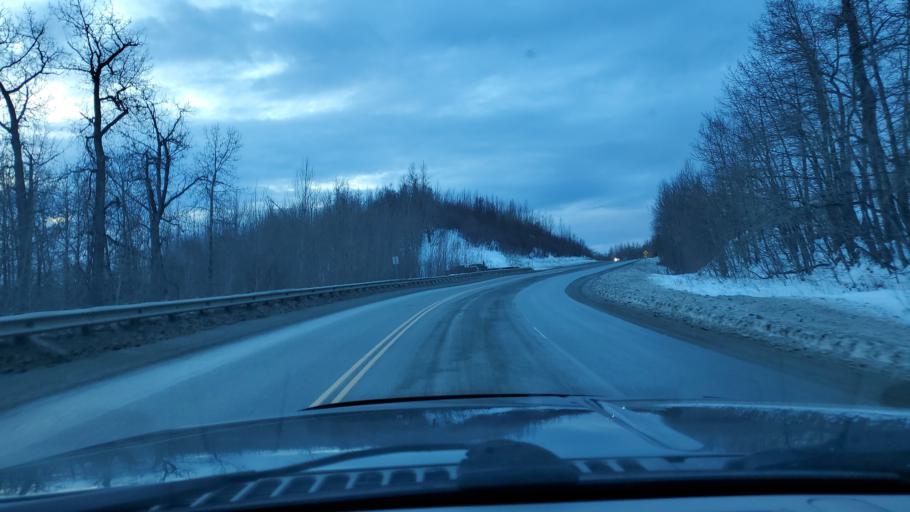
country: US
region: Alaska
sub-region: Matanuska-Susitna Borough
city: Lazy Mountain
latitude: 61.6963
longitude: -148.9566
